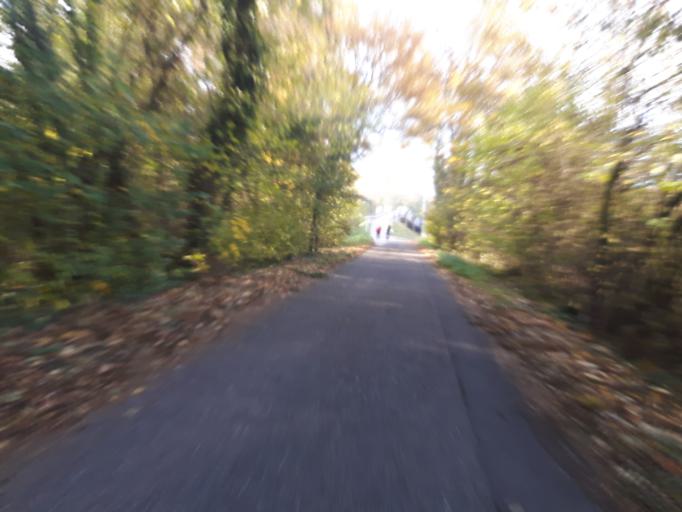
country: DE
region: Baden-Wuerttemberg
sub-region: Karlsruhe Region
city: Malsch
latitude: 49.2620
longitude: 8.6592
